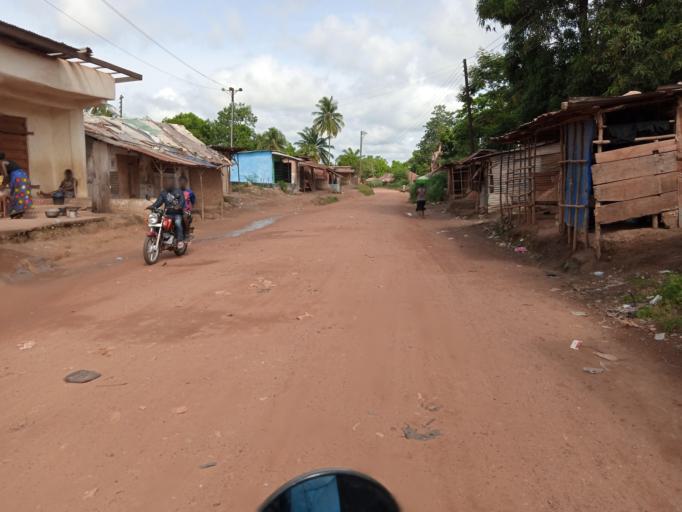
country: SL
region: Southern Province
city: Bo
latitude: 7.9597
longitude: -11.7450
